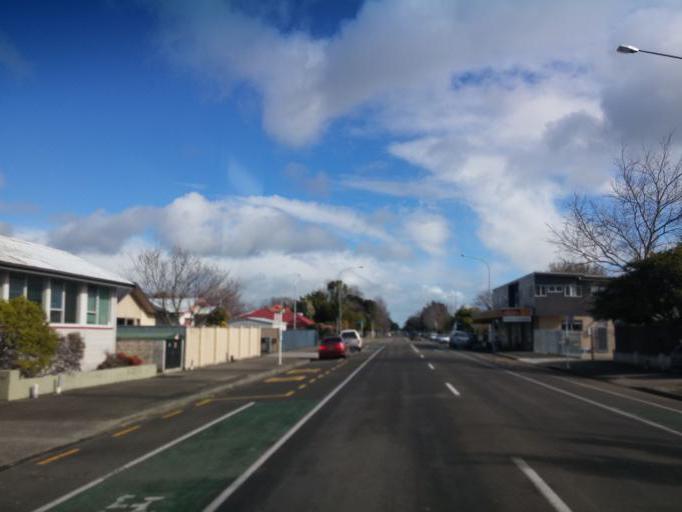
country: NZ
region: Manawatu-Wanganui
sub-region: Palmerston North City
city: Palmerston North
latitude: -40.3606
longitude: 175.6194
